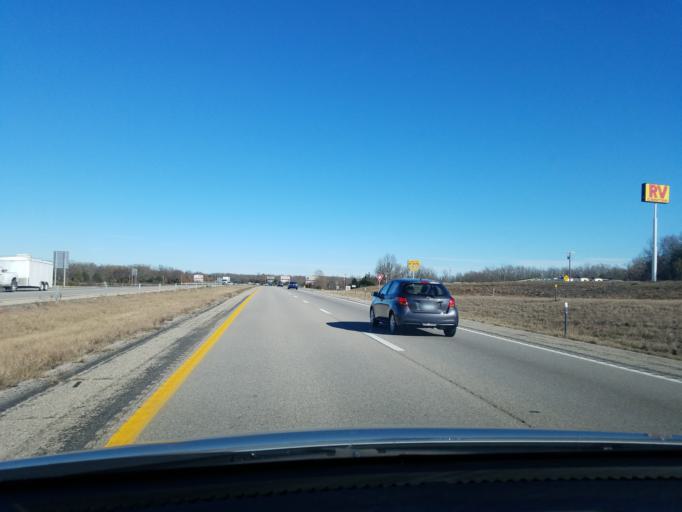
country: US
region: Missouri
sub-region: Laclede County
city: Lebanon
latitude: 37.6005
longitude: -92.7136
